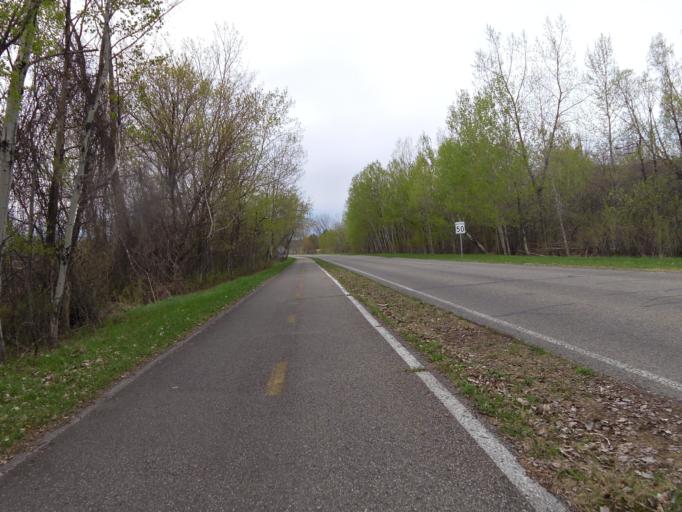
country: CA
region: Quebec
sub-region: Laurentides
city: Oka
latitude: 45.4783
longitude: -74.0504
